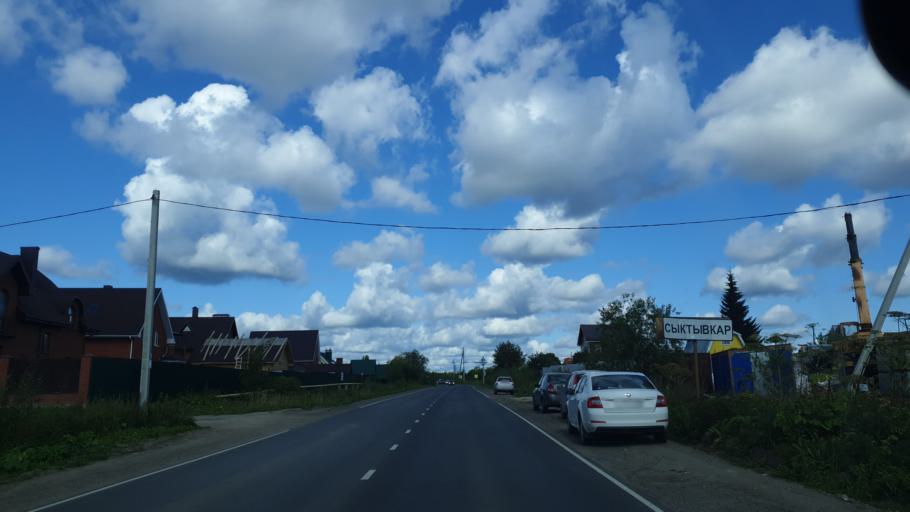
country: RU
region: Komi Republic
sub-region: Syktyvdinskiy Rayon
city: Syktyvkar
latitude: 61.6366
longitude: 50.8030
